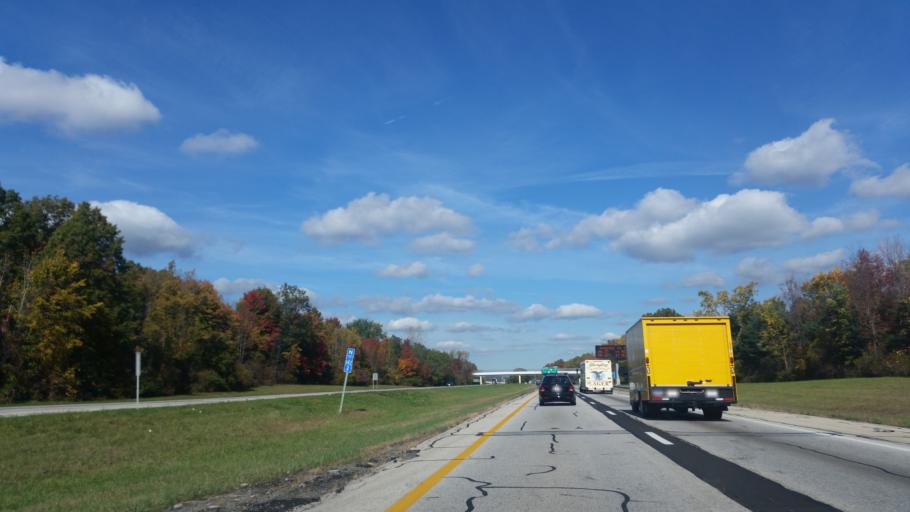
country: US
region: Ohio
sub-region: Summit County
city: Richfield
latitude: 41.2075
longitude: -81.6255
